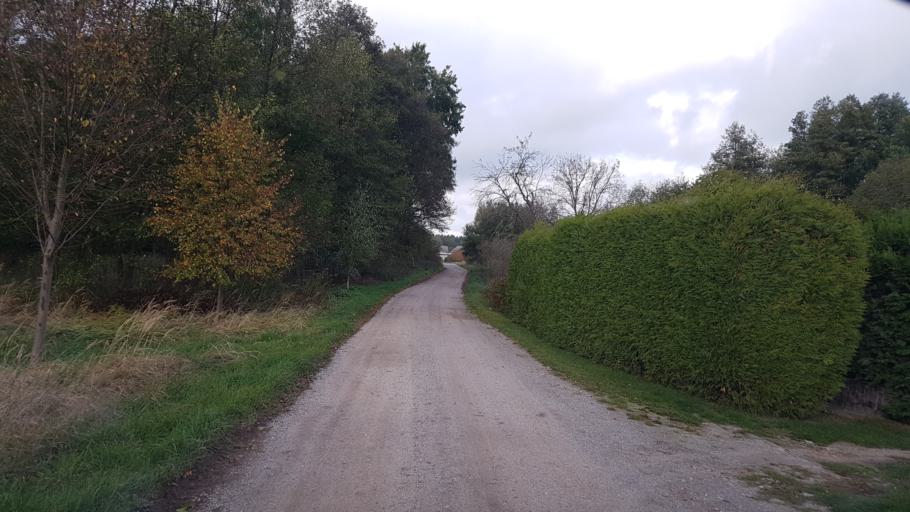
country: DE
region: Brandenburg
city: Schonborn
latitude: 51.6142
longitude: 13.5151
